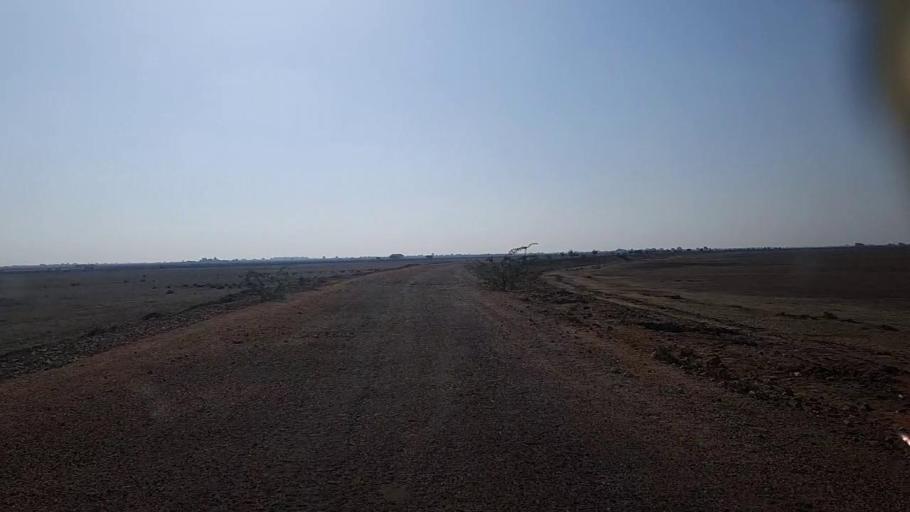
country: PK
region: Sindh
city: Mirpur Sakro
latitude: 24.5151
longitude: 67.5043
